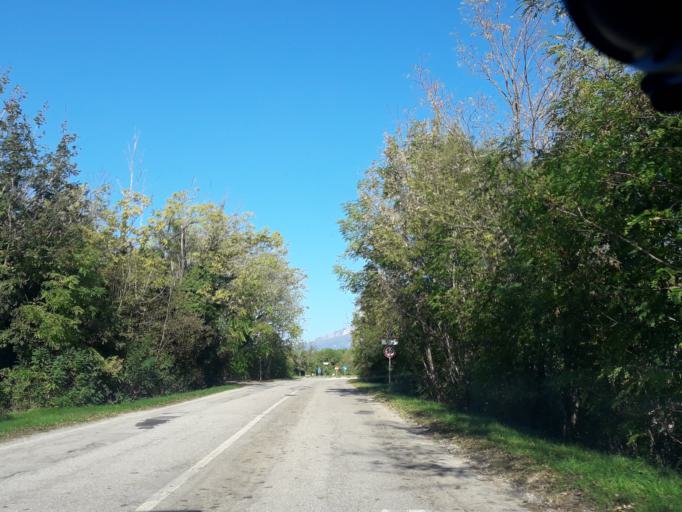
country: IT
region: Friuli Venezia Giulia
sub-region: Provincia di Udine
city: Povoletto
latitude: 46.1094
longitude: 13.2722
